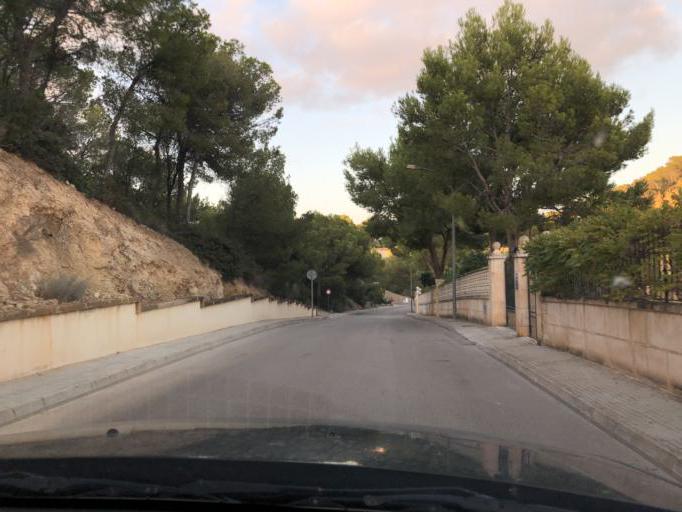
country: ES
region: Balearic Islands
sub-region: Illes Balears
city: Santa Ponsa
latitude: 39.5285
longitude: 2.4659
